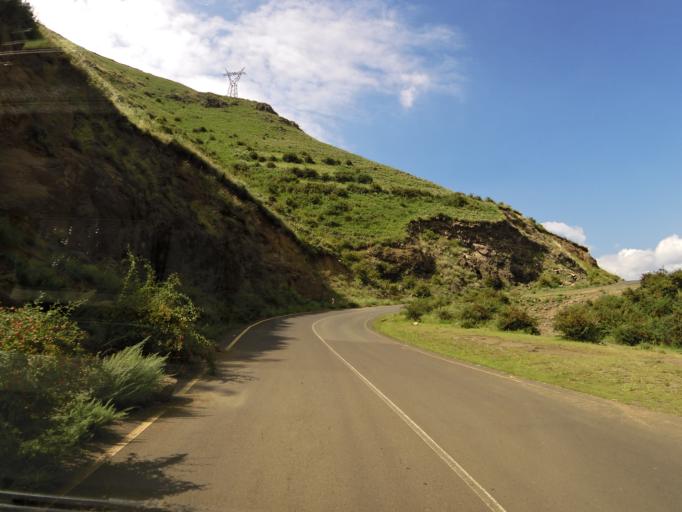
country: LS
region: Thaba-Tseka
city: Thaba-Tseka
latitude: -29.1409
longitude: 28.4889
